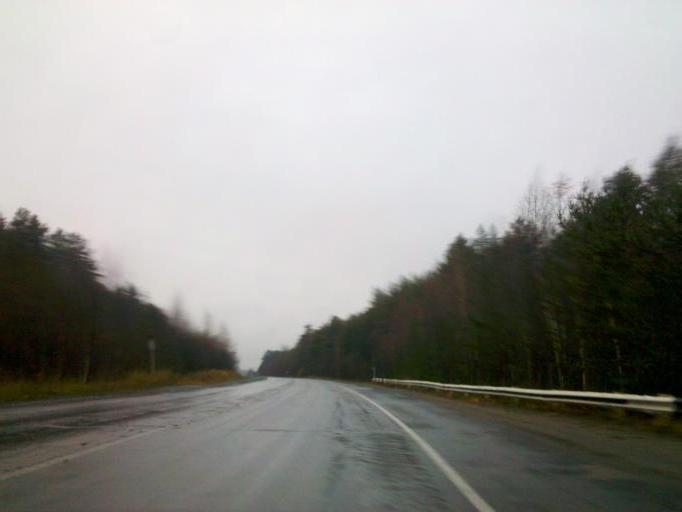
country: RU
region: Republic of Karelia
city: Shuya
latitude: 61.8571
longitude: 34.1763
